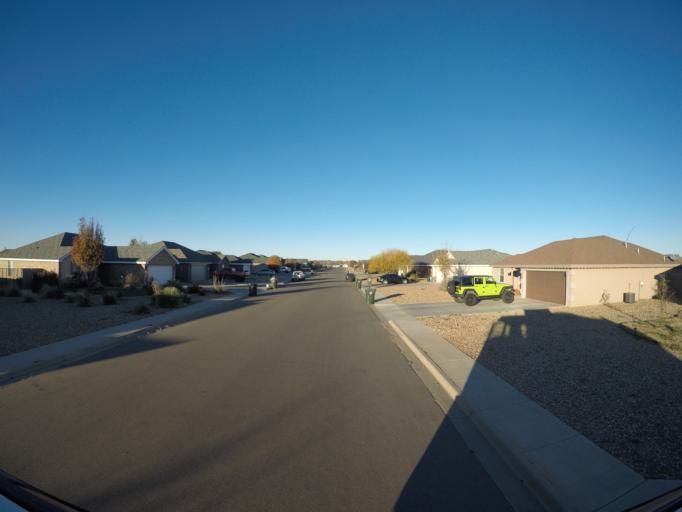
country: US
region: New Mexico
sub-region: Curry County
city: Clovis
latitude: 34.4082
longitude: -103.1694
